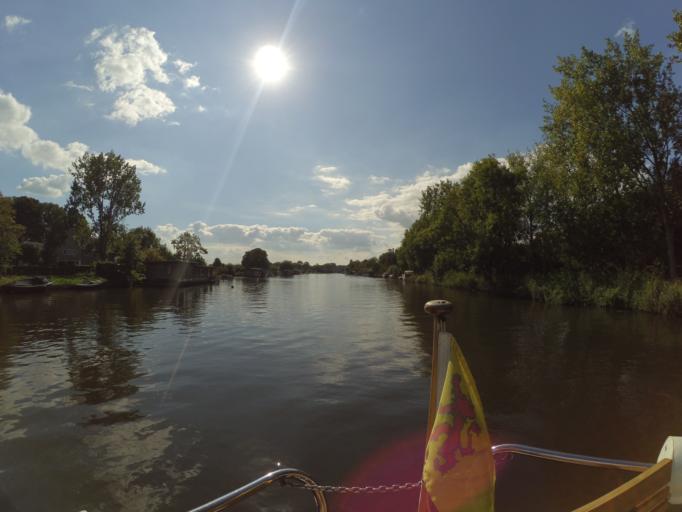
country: NL
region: Utrecht
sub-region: Stichtse Vecht
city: Vreeland
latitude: 52.2152
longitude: 5.0312
